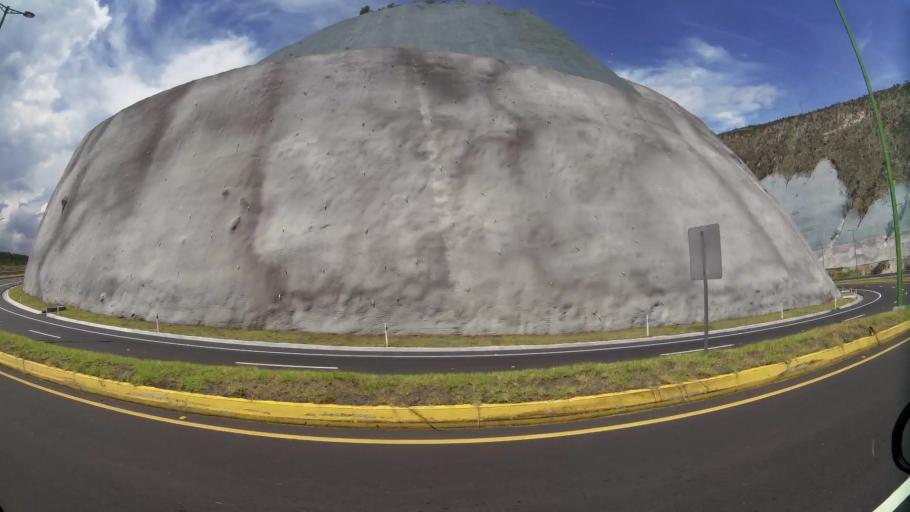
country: EC
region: Pichincha
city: Quito
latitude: -0.0989
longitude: -78.3852
